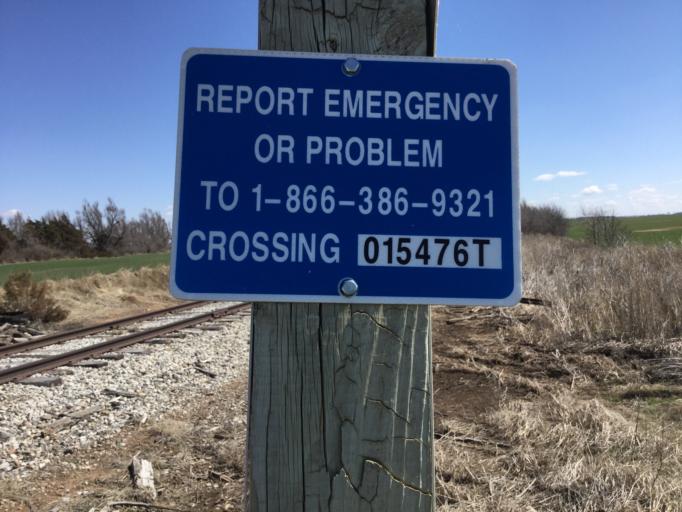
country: US
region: Kansas
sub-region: Barber County
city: Medicine Lodge
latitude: 37.4631
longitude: -98.5378
